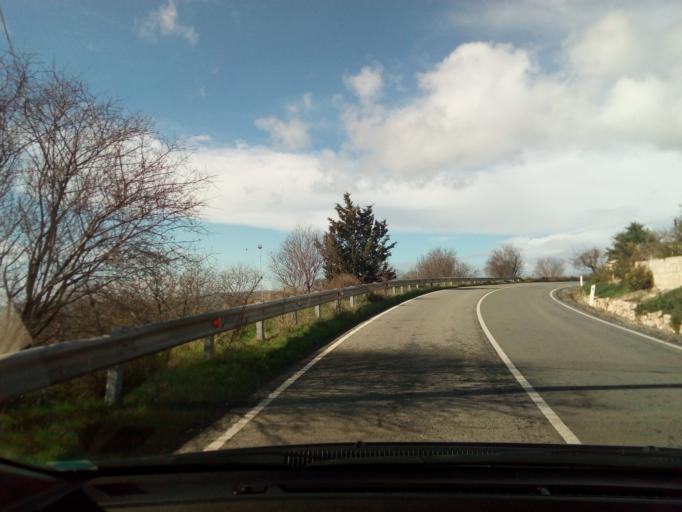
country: CY
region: Pafos
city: Tala
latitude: 34.9179
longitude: 32.5311
